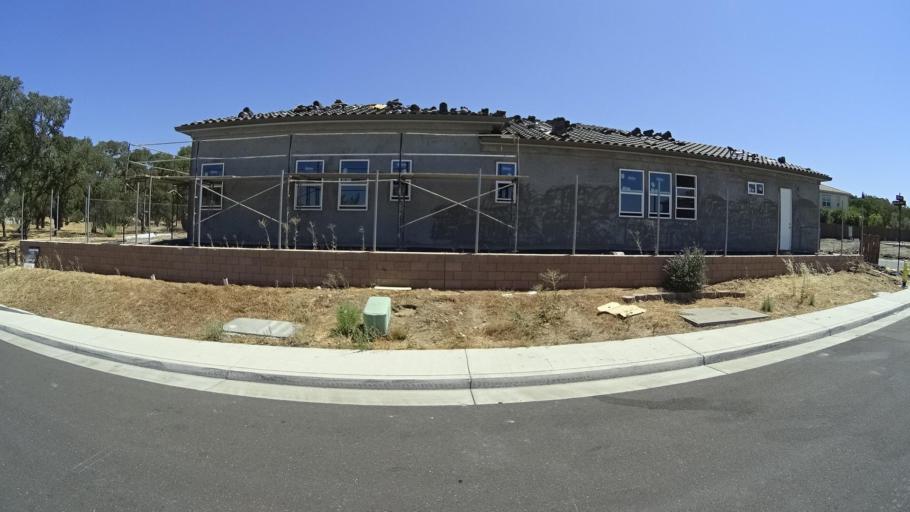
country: US
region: California
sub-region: Placer County
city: Rocklin
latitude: 38.8345
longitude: -121.2511
